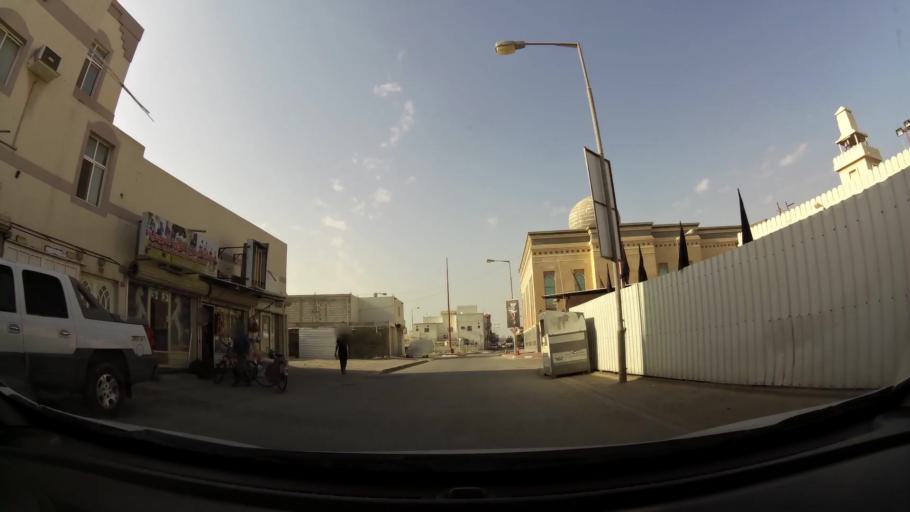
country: BH
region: Manama
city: Jidd Hafs
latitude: 26.2135
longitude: 50.5128
